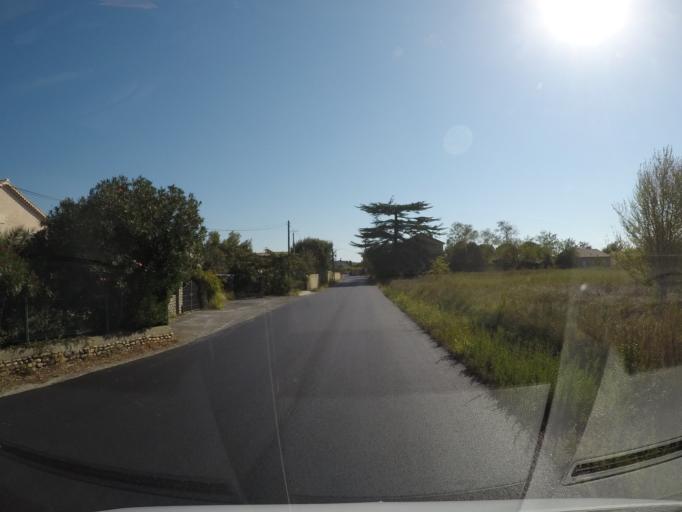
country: FR
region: Languedoc-Roussillon
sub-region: Departement du Gard
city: Ribaute-les-Tavernes
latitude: 44.0242
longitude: 4.0837
